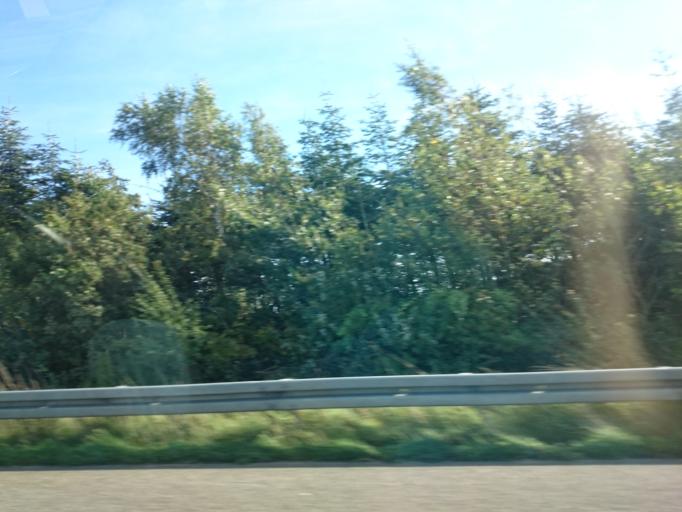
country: DK
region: Central Jutland
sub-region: Horsens Kommune
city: Horsens
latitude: 55.9623
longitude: 9.8438
